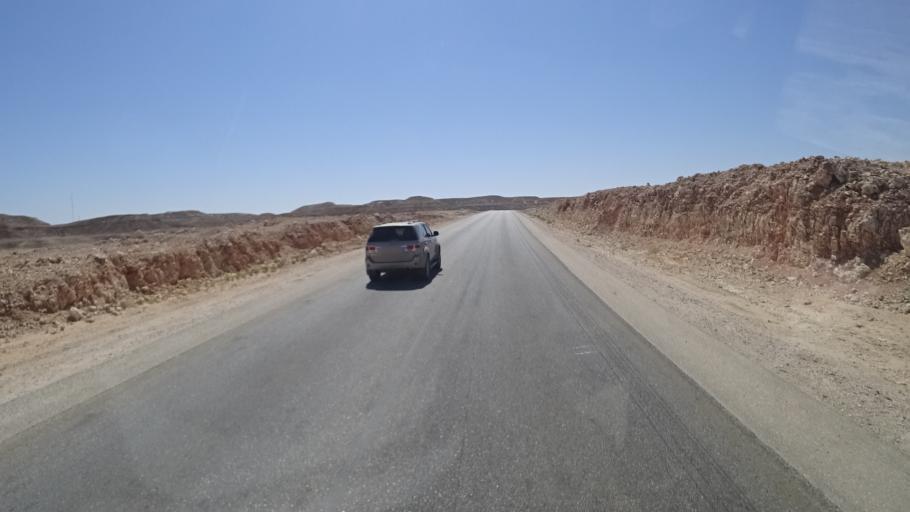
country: OM
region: Zufar
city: Salalah
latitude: 17.4939
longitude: 53.3618
